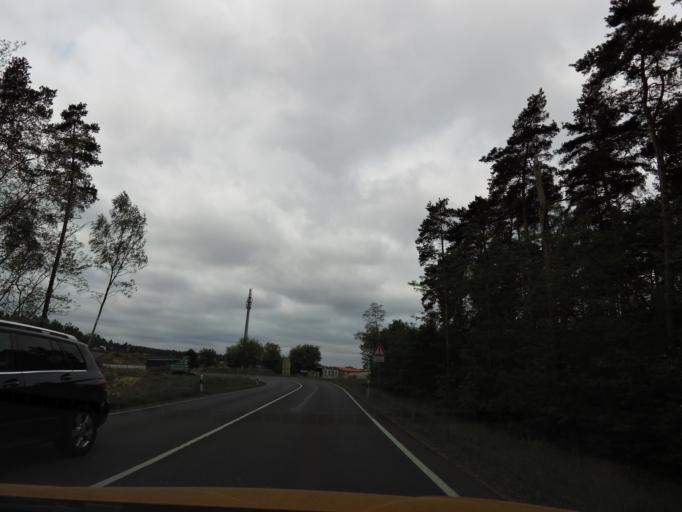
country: DE
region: Brandenburg
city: Michendorf
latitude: 52.3011
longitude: 13.0278
